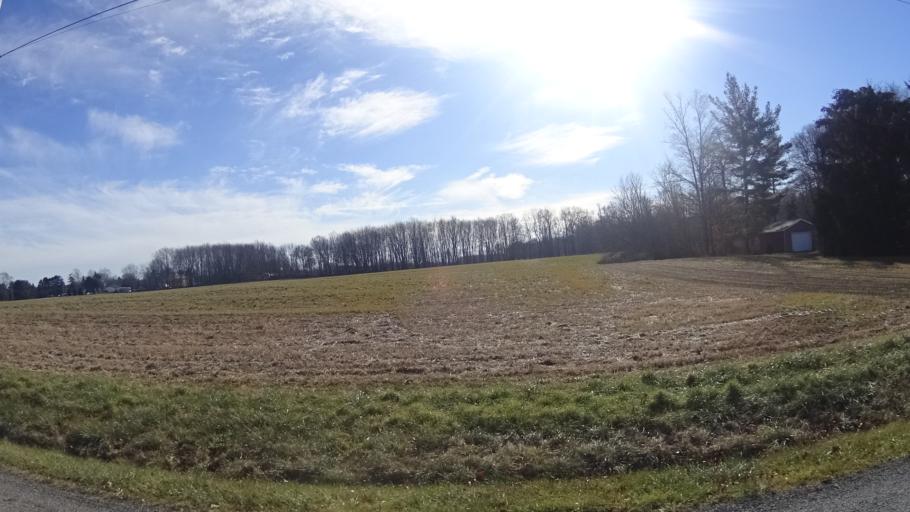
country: US
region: Ohio
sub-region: Lorain County
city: South Amherst
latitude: 41.3194
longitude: -82.3204
